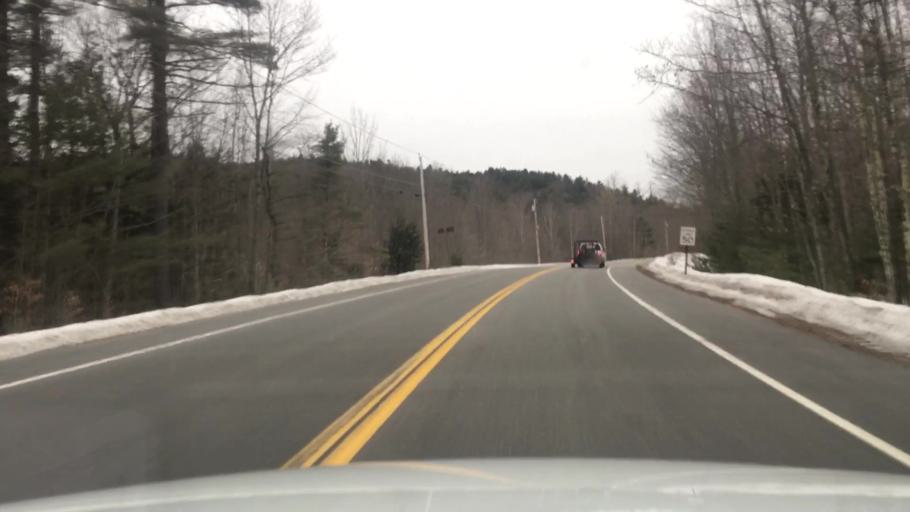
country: US
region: Maine
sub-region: York County
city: Limerick
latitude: 43.7356
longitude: -70.8168
